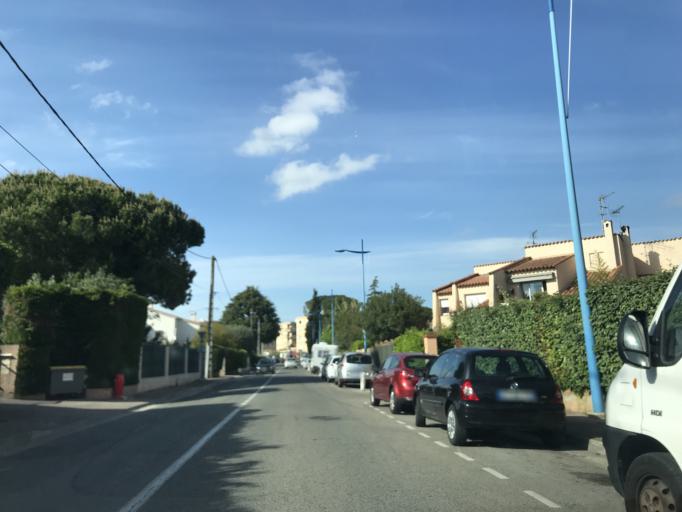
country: FR
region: Provence-Alpes-Cote d'Azur
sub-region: Departement des Alpes-Maritimes
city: Mandelieu-la-Napoule
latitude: 43.5399
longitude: 6.9420
